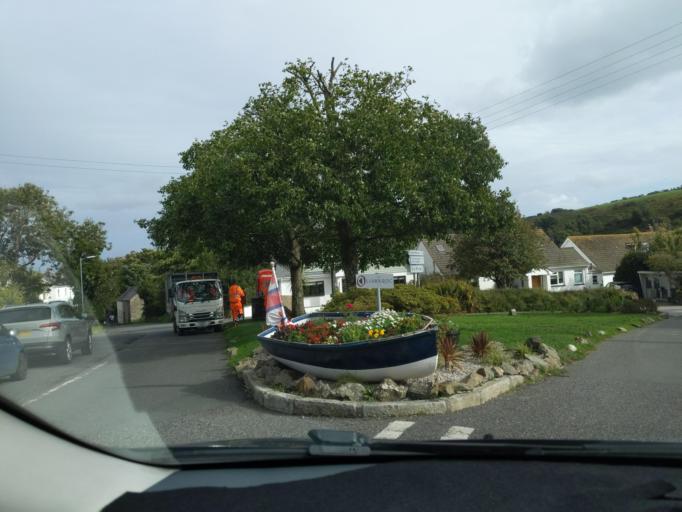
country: GB
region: England
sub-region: Cornwall
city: Mevagissey
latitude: 50.2404
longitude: -4.7962
